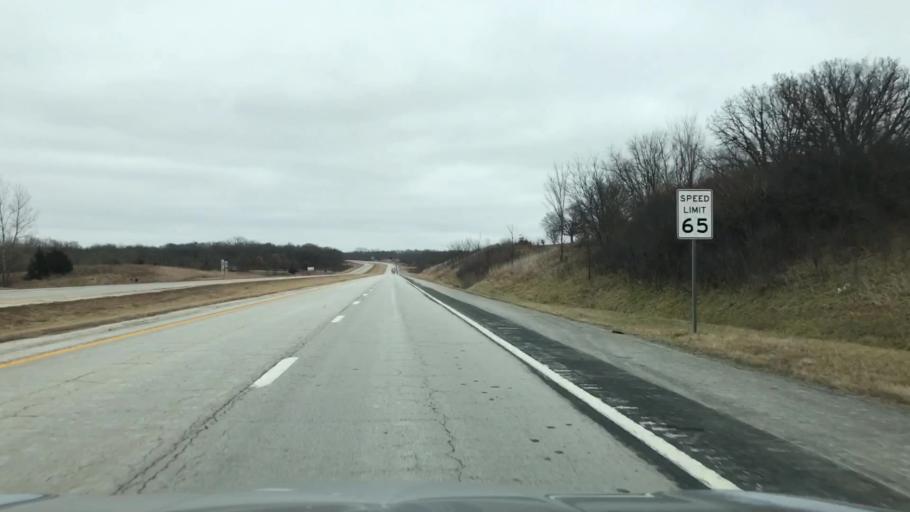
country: US
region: Missouri
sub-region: Caldwell County
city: Hamilton
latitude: 39.7411
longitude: -94.0372
